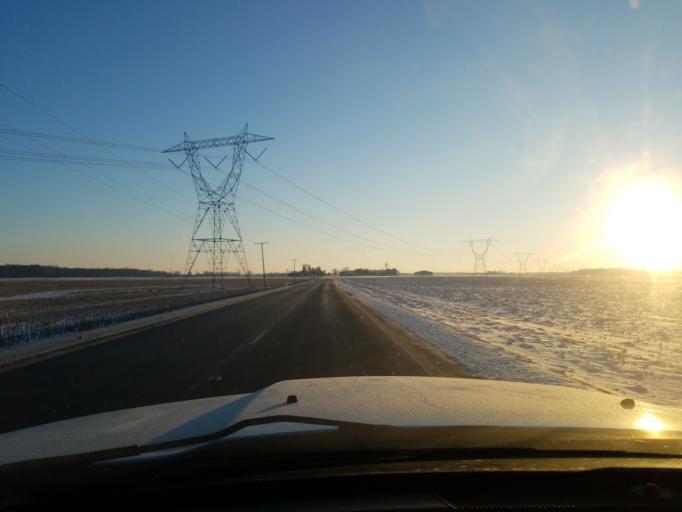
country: US
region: Indiana
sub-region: Marshall County
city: Bremen
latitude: 41.4499
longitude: -86.2313
